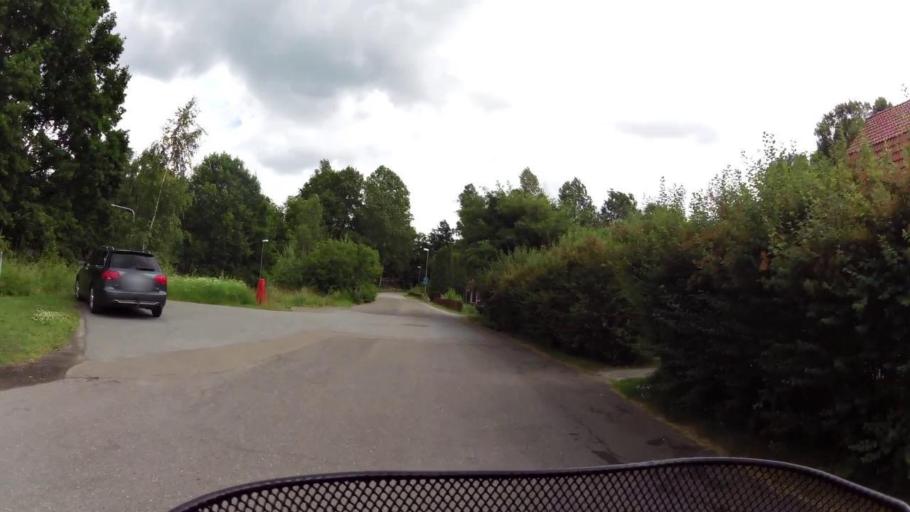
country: SE
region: OEstergoetland
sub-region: Linkopings Kommun
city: Malmslatt
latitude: 58.4130
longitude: 15.5252
